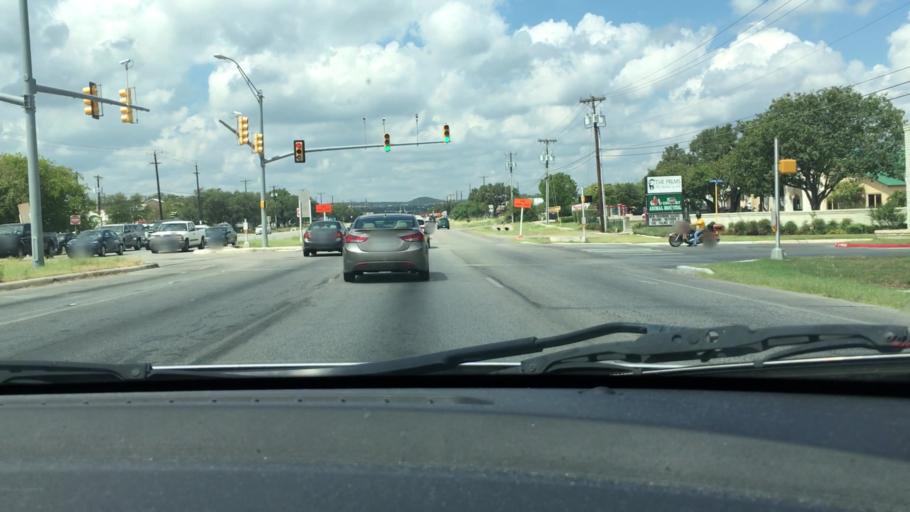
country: US
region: Texas
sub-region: Bexar County
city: Helotes
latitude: 29.5589
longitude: -98.6743
